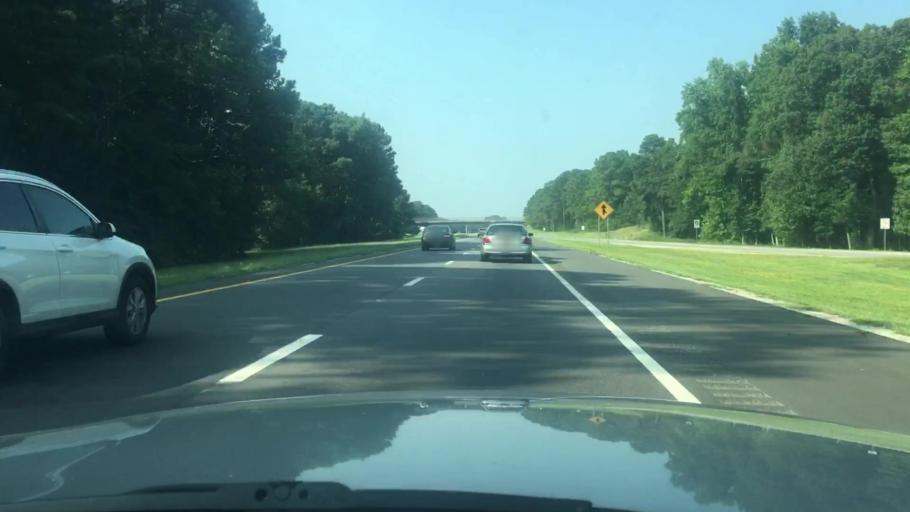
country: US
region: North Carolina
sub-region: Cumberland County
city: Vander
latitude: 34.9936
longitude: -78.8342
